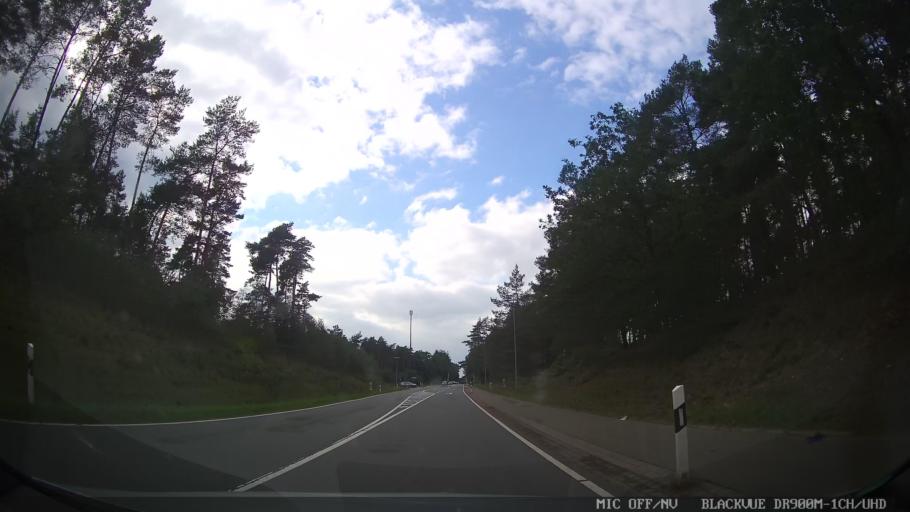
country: DE
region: Lower Saxony
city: Soltau
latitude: 52.9868
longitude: 9.9303
